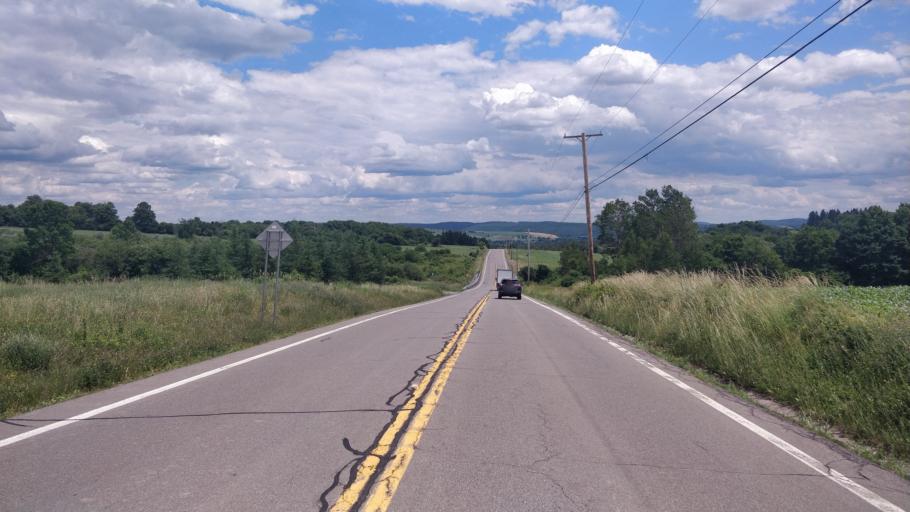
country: US
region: New York
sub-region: Cortland County
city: Homer
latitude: 42.6397
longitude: -76.2216
